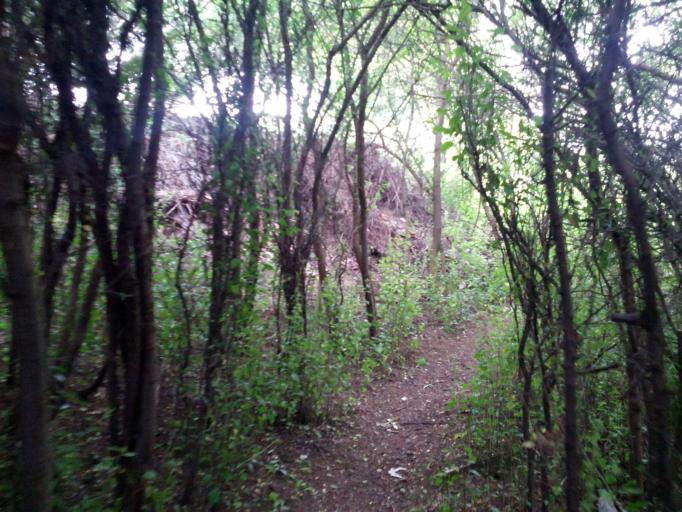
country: DE
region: Thuringia
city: Eisenach
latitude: 50.9855
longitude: 10.3328
